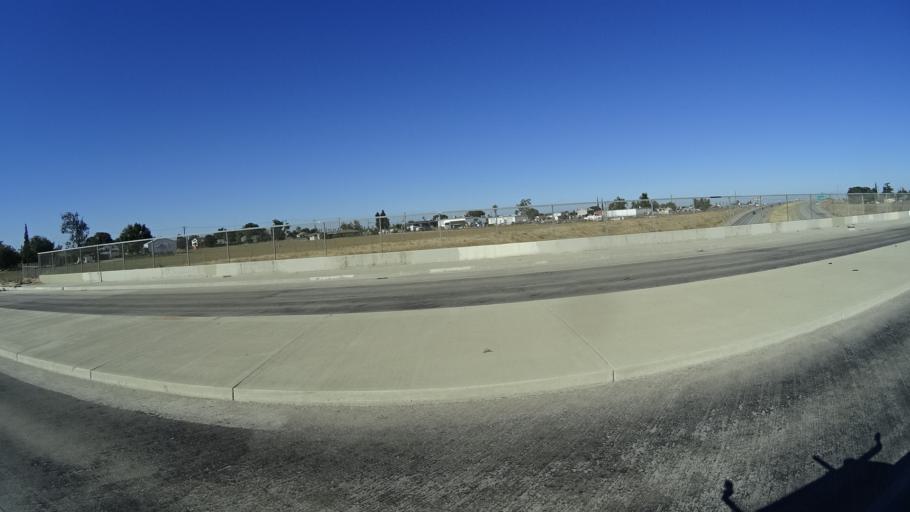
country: US
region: California
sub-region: Fresno County
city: West Park
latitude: 36.7382
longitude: -119.8316
